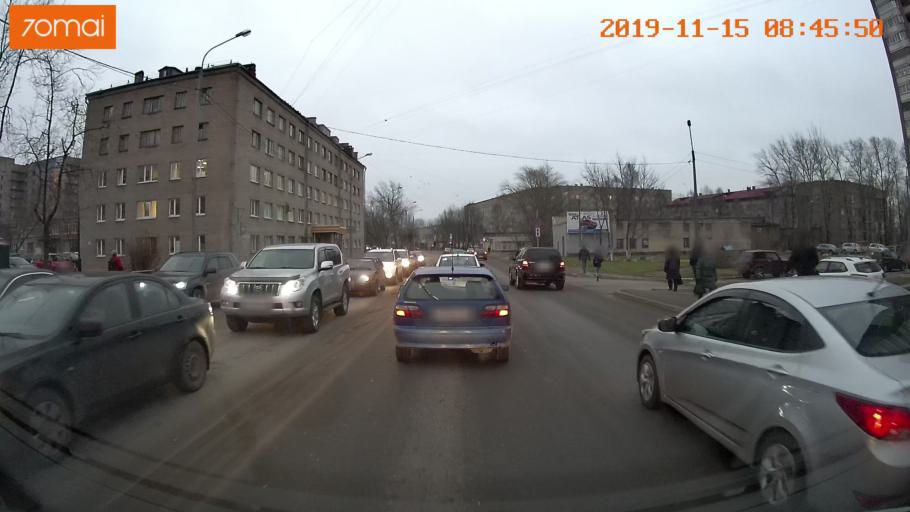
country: RU
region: Vologda
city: Cherepovets
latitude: 59.1190
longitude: 37.9041
